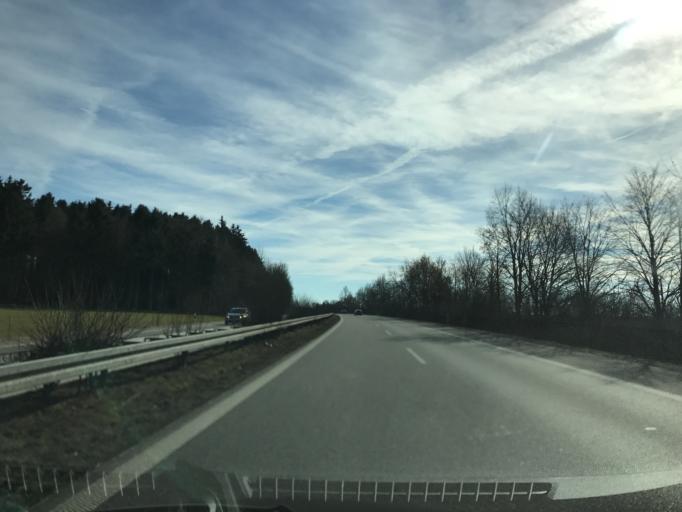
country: DE
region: Baden-Wuerttemberg
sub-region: Tuebingen Region
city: Warthausen
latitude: 48.1290
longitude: 9.8227
